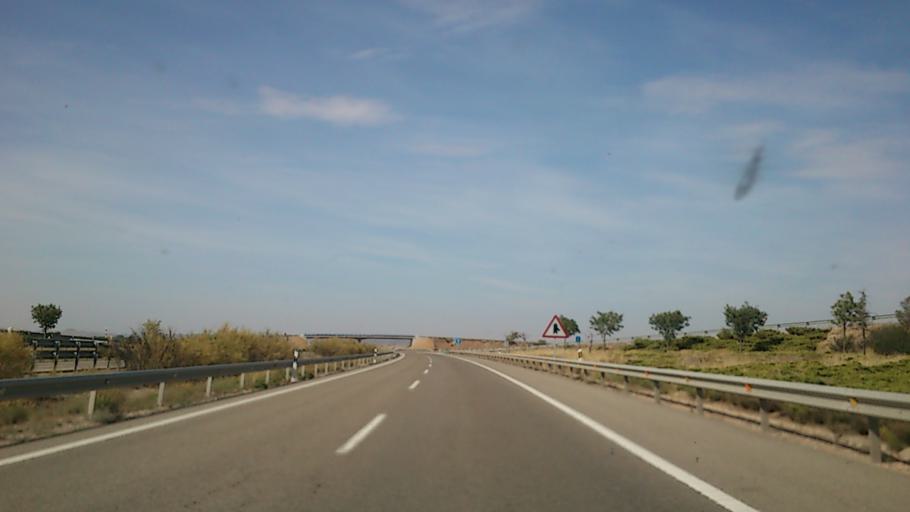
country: ES
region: Aragon
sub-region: Provincia de Teruel
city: Caminreal
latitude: 40.8387
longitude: -1.3104
